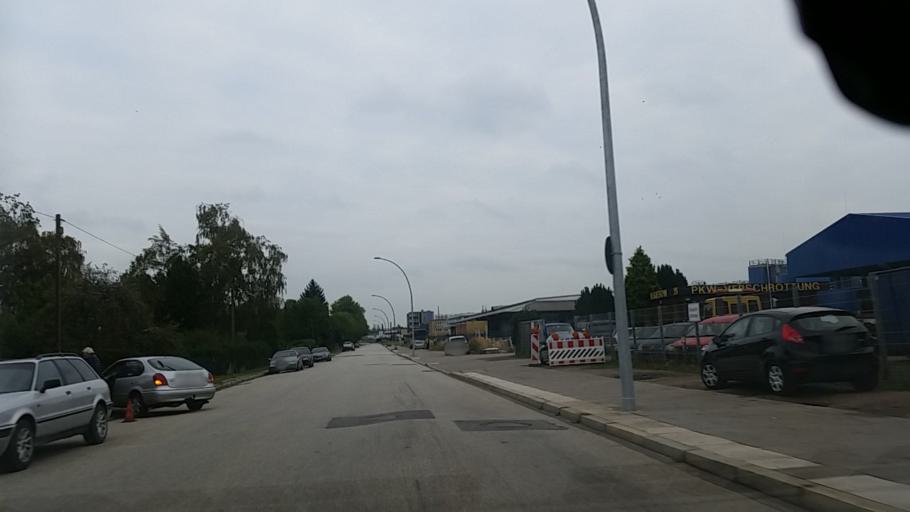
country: DE
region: Hamburg
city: Rothenburgsort
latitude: 53.5253
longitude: 10.0757
